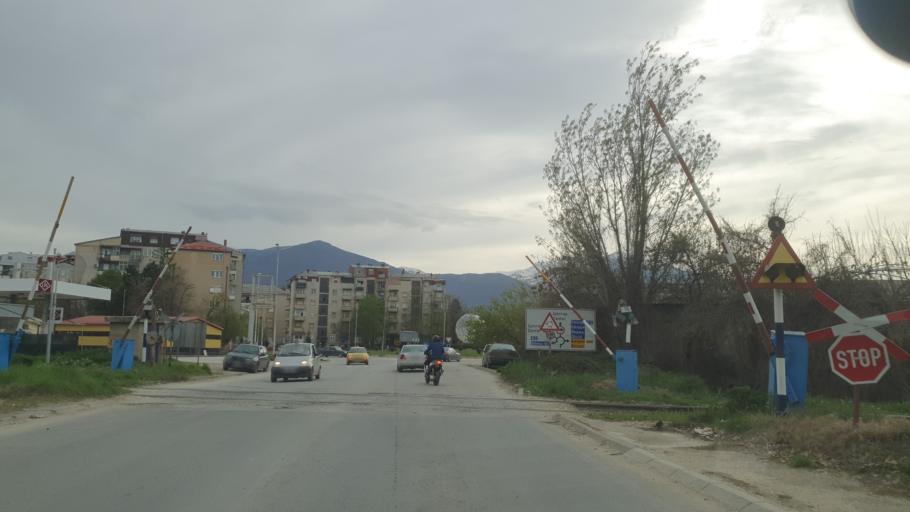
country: MK
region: Bitola
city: Gorno Orizari
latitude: 41.0385
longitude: 21.3481
